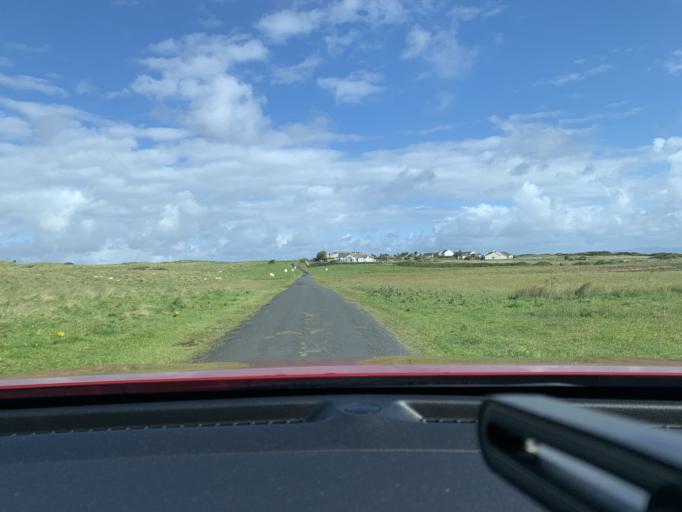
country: IE
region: Connaught
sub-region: Sligo
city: Strandhill
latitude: 54.4000
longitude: -8.5640
